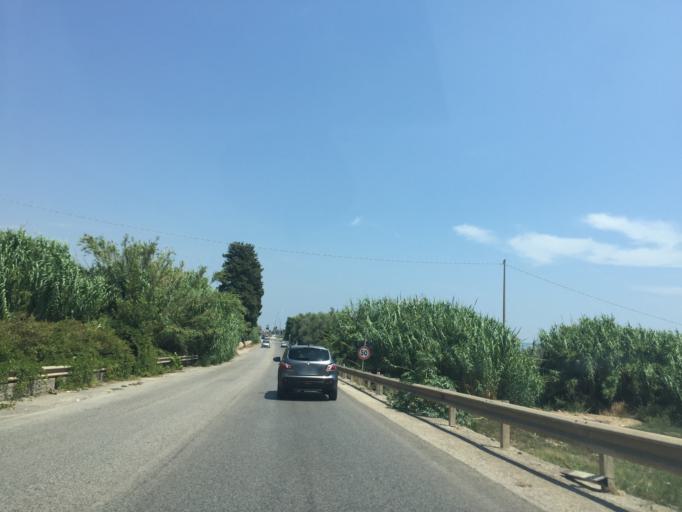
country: IT
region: Sicily
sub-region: Provincia di Siracusa
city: Avola
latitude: 36.9220
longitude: 15.1531
